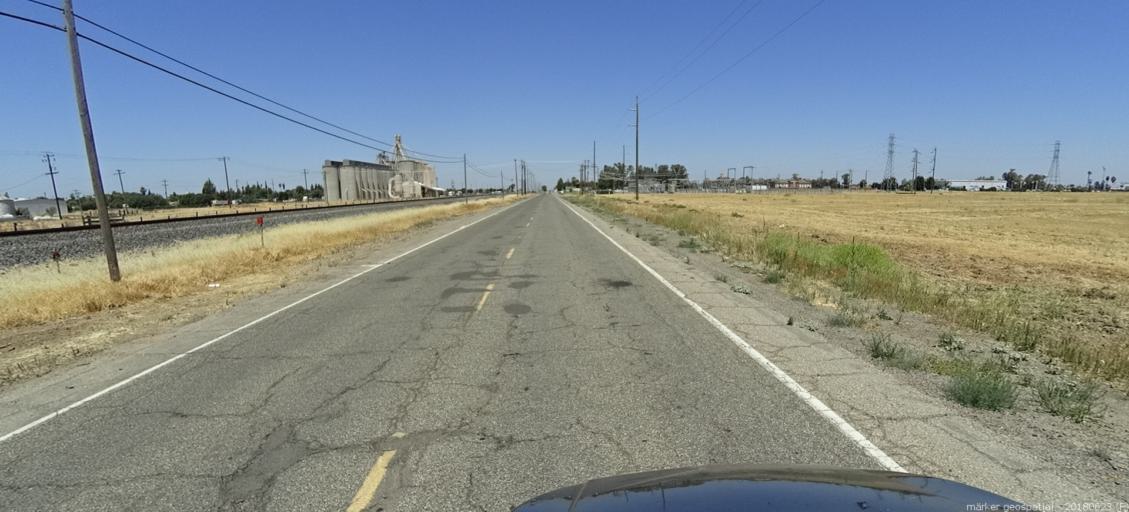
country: US
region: California
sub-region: Madera County
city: Chowchilla
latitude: 37.1187
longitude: -120.2494
